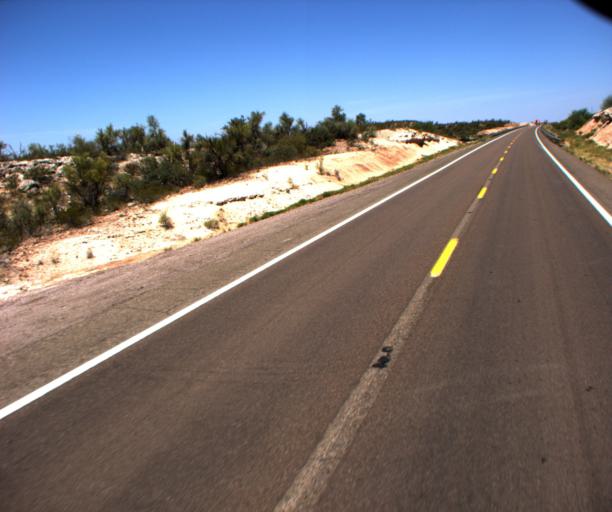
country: US
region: Arizona
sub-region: Graham County
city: Bylas
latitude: 33.2091
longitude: -110.2038
